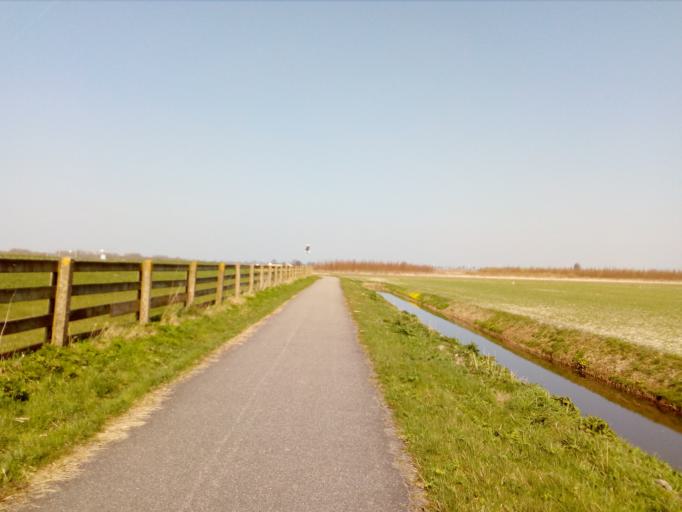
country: NL
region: South Holland
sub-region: Gemeente Waddinxveen
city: Groenswaard
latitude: 52.0646
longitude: 4.6082
